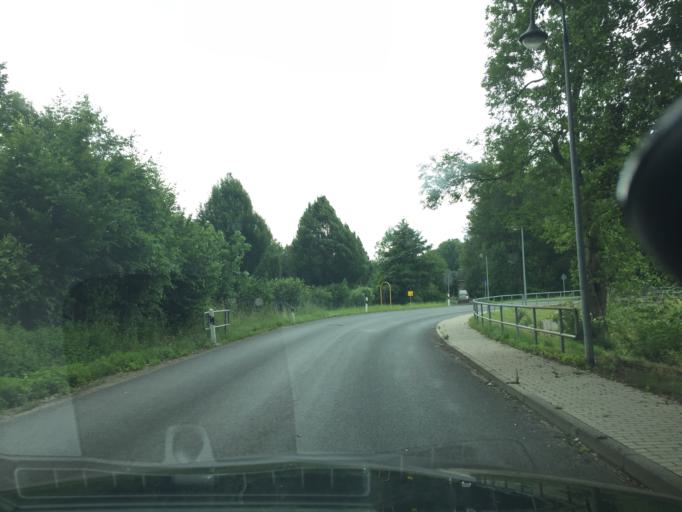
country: DE
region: Thuringia
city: Schmolln
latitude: 50.8889
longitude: 12.3413
